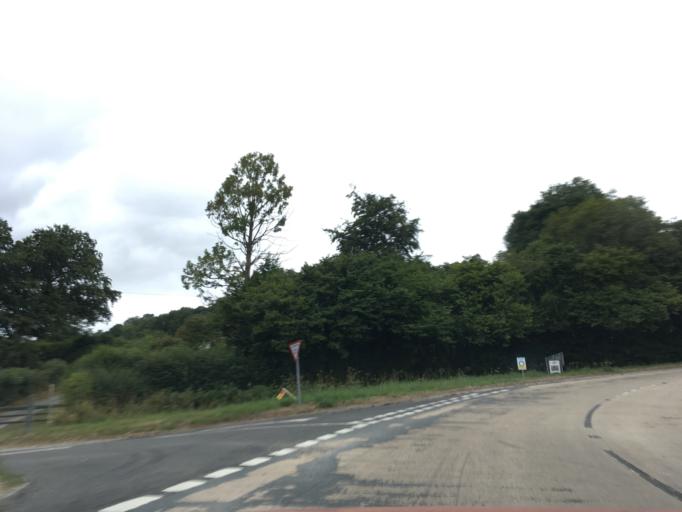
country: GB
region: Wales
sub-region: Blaenau Gwent
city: Brynmawr
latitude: 51.8828
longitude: -3.2352
